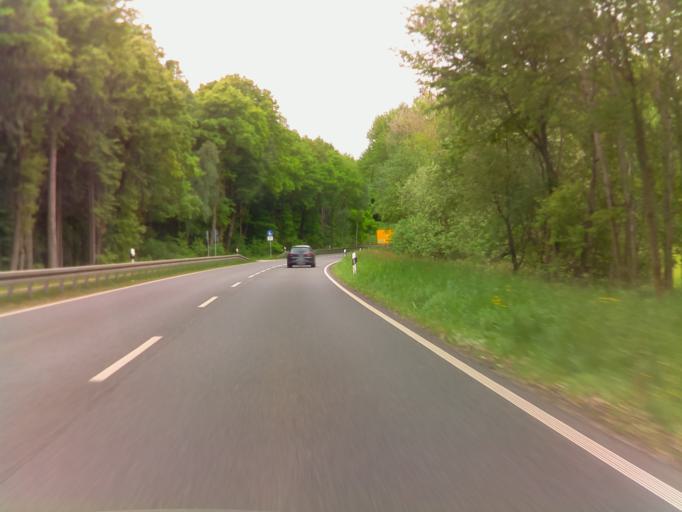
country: DE
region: Hesse
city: Stadtallendorf
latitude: 50.8347
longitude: 9.0586
